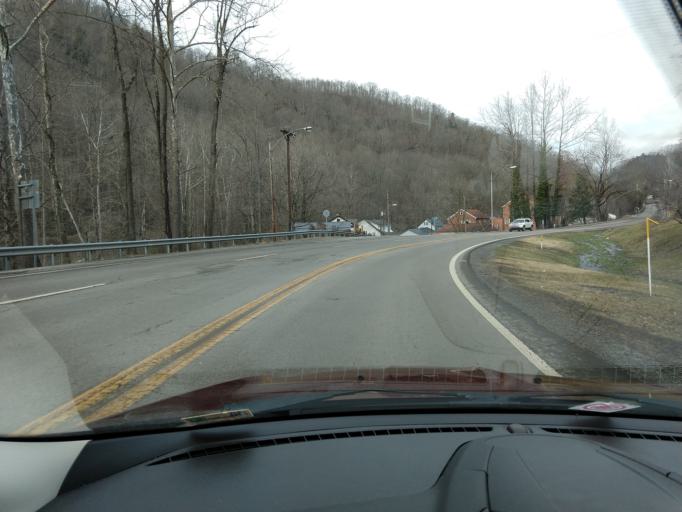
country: US
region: West Virginia
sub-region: McDowell County
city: Welch
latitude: 37.4207
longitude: -81.5894
